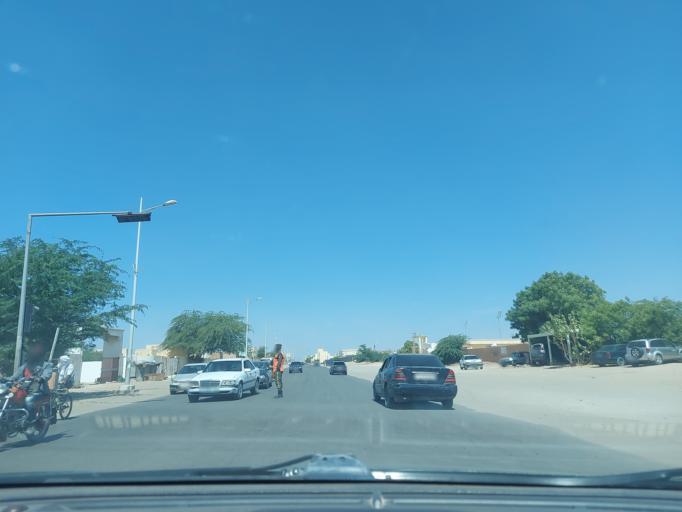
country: MR
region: Nouakchott
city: Nouakchott
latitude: 18.0800
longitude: -15.9687
